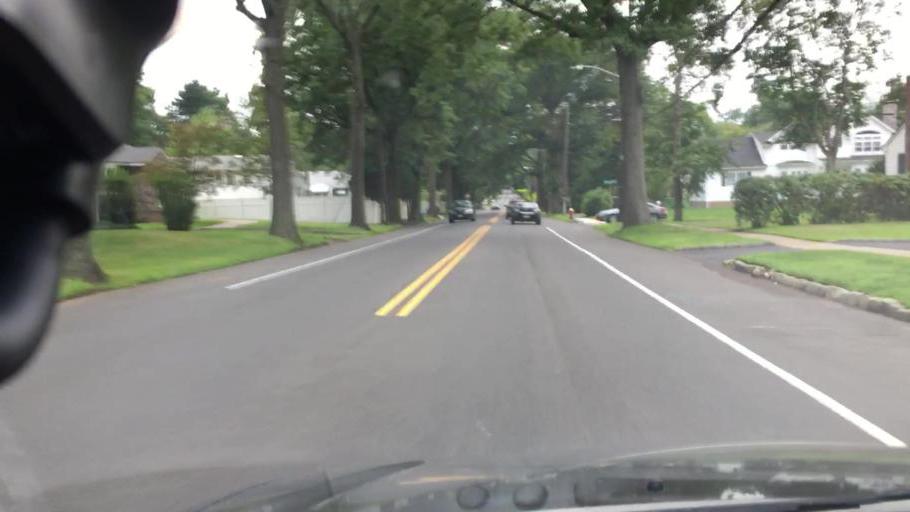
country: US
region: New Jersey
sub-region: Union County
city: Clark
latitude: 40.6367
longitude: -74.3204
